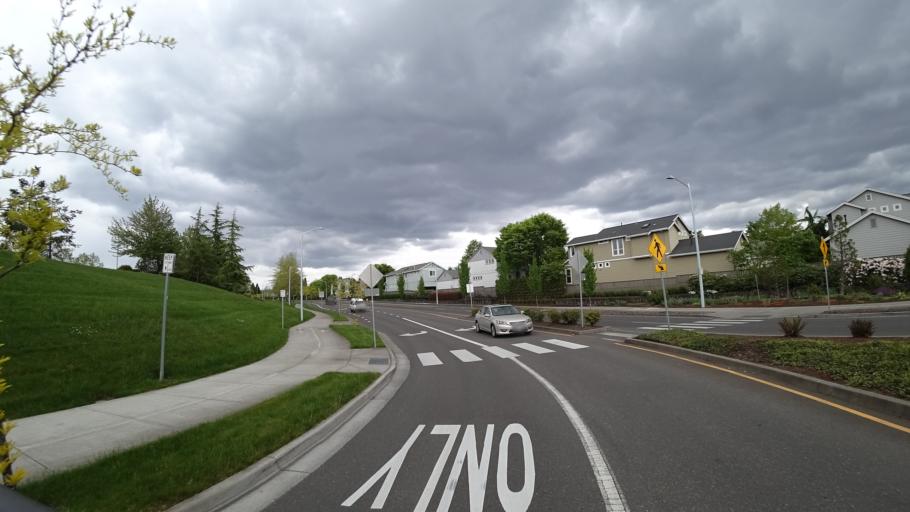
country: US
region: Oregon
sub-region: Washington County
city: Rockcreek
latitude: 45.5384
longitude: -122.9135
